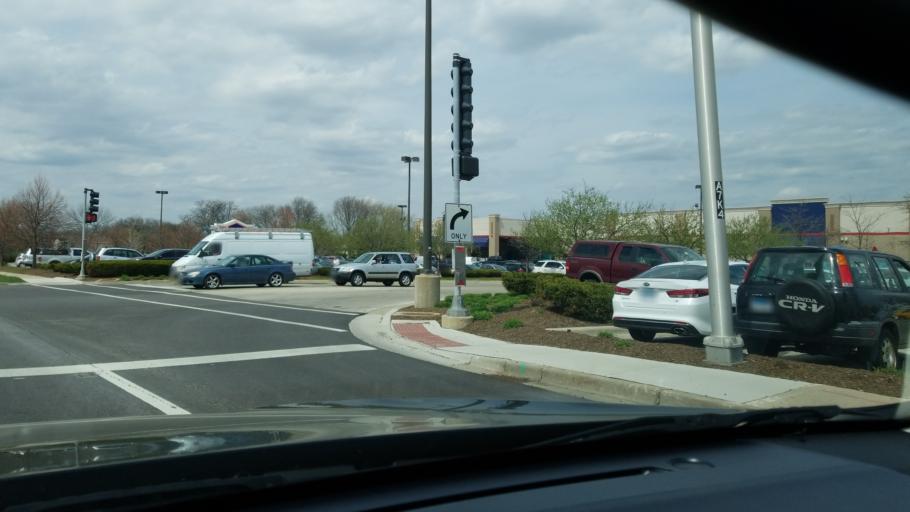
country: US
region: Illinois
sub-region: Cook County
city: Rolling Meadows
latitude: 42.0530
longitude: -87.9959
